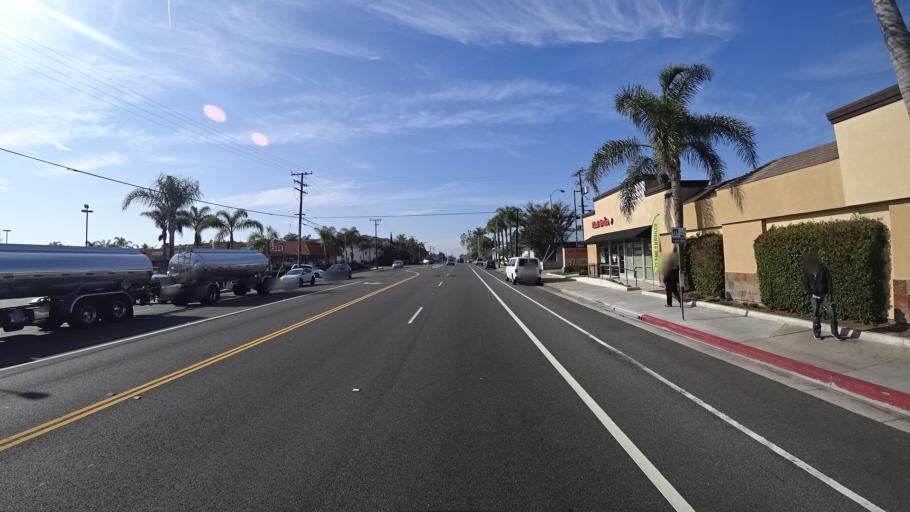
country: US
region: California
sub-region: Orange County
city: Fountain Valley
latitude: 33.7013
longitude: -117.9896
